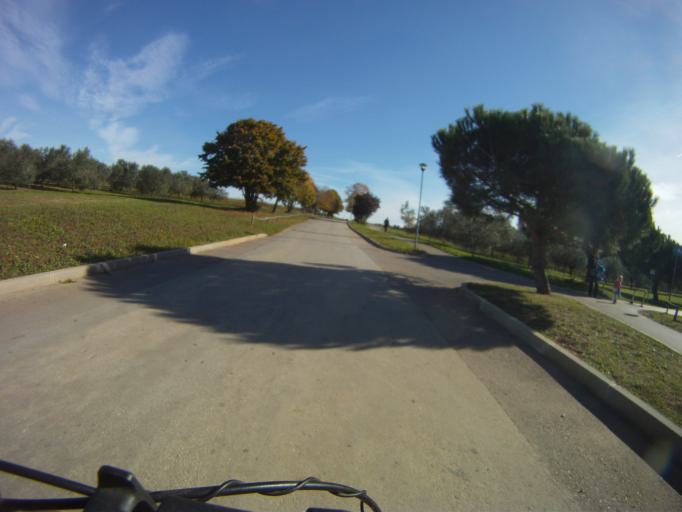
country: HR
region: Istarska
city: Novigrad
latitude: 45.3257
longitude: 13.5524
